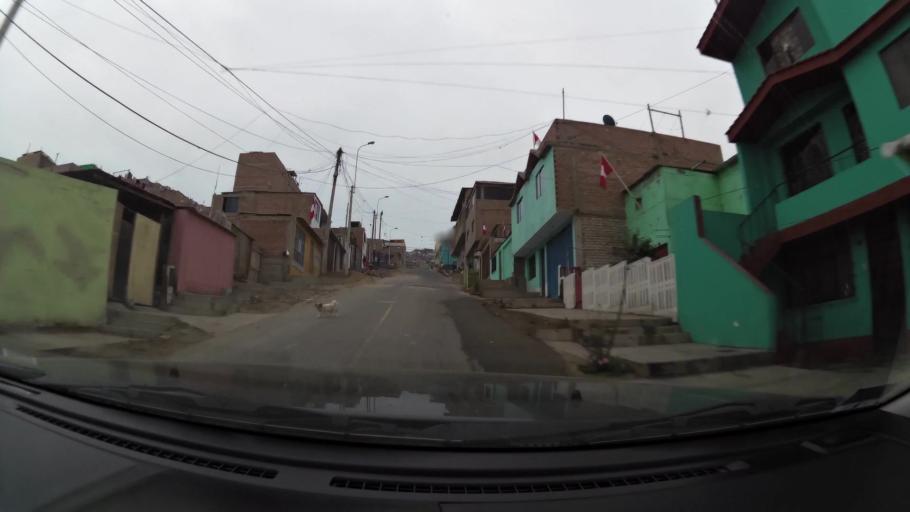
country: PE
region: Lima
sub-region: Lima
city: Surco
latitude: -12.1980
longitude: -77.0265
